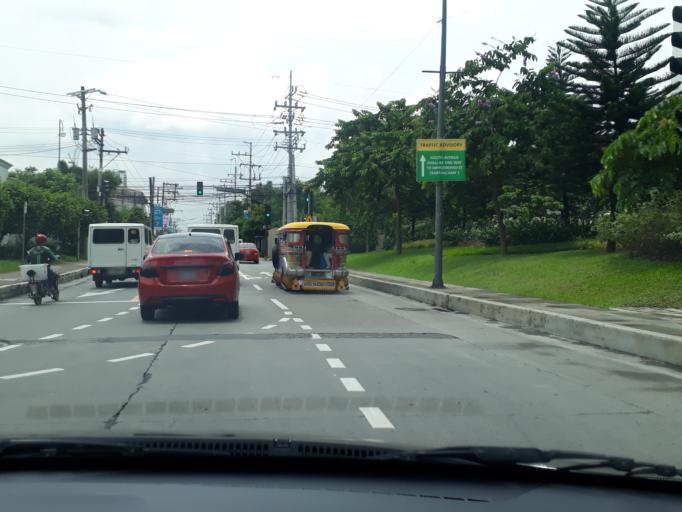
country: PH
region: Metro Manila
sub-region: Makati City
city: Makati City
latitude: 14.5638
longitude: 121.0161
